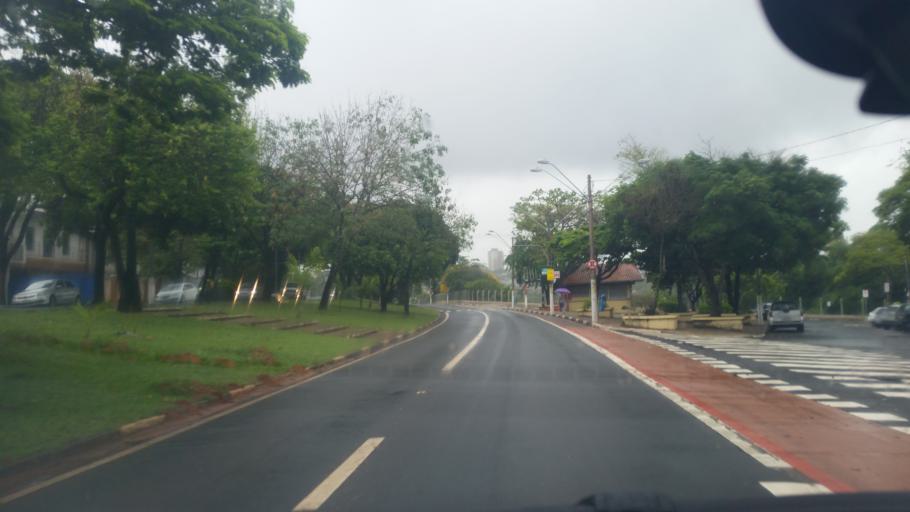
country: BR
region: Sao Paulo
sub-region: Campinas
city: Campinas
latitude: -22.8774
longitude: -47.0577
